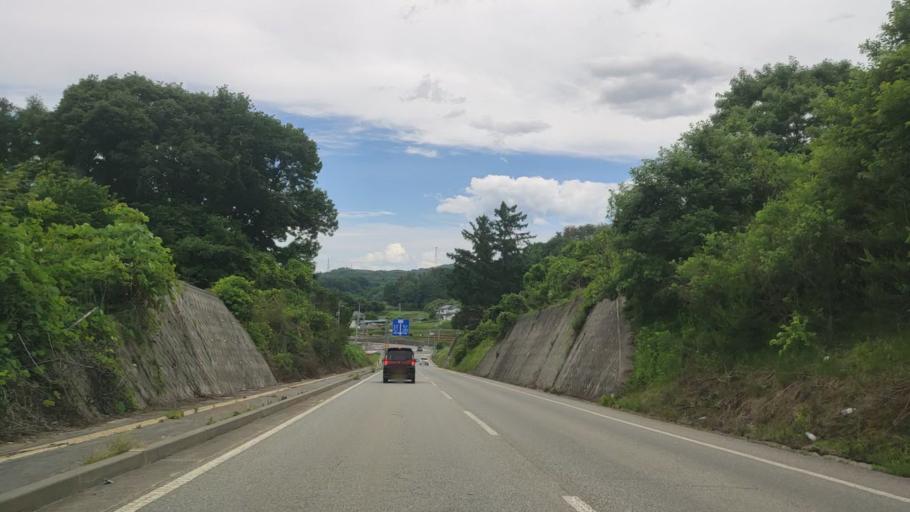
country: JP
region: Nagano
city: Kamimaruko
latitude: 36.2718
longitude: 138.3053
